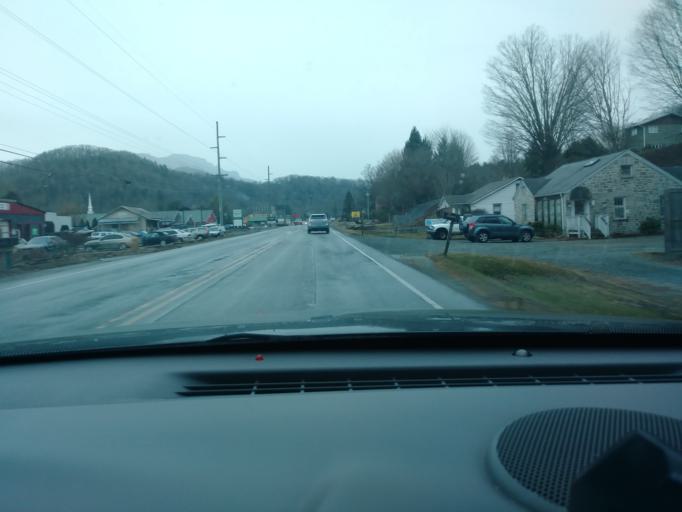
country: US
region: North Carolina
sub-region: Watauga County
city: Foscoe
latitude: 36.1600
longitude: -81.7680
